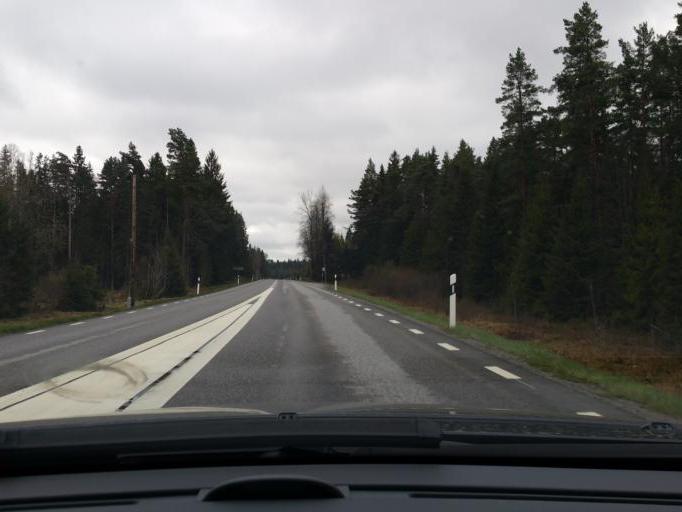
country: SE
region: Kronoberg
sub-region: Vaxjo Kommun
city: Lammhult
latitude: 57.1495
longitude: 14.5965
